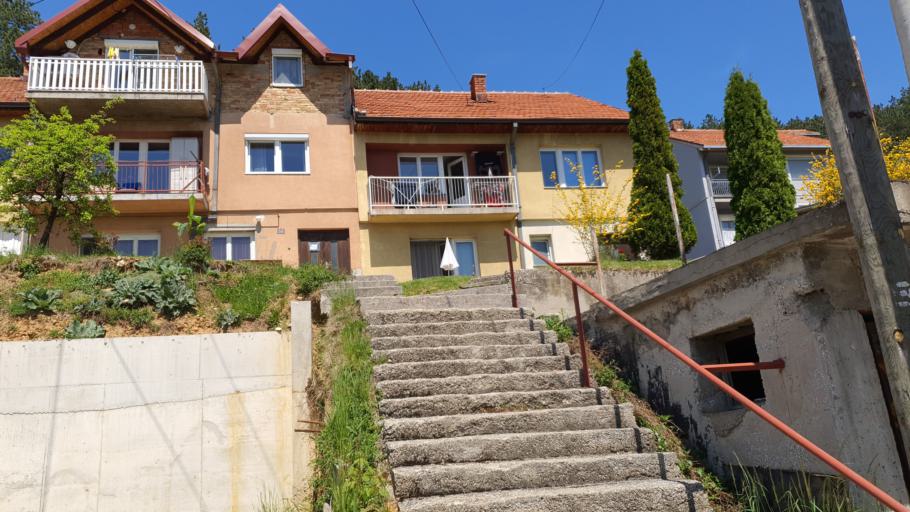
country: RS
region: Central Serbia
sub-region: Zlatiborski Okrug
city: Uzice
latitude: 43.8605
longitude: 19.8444
